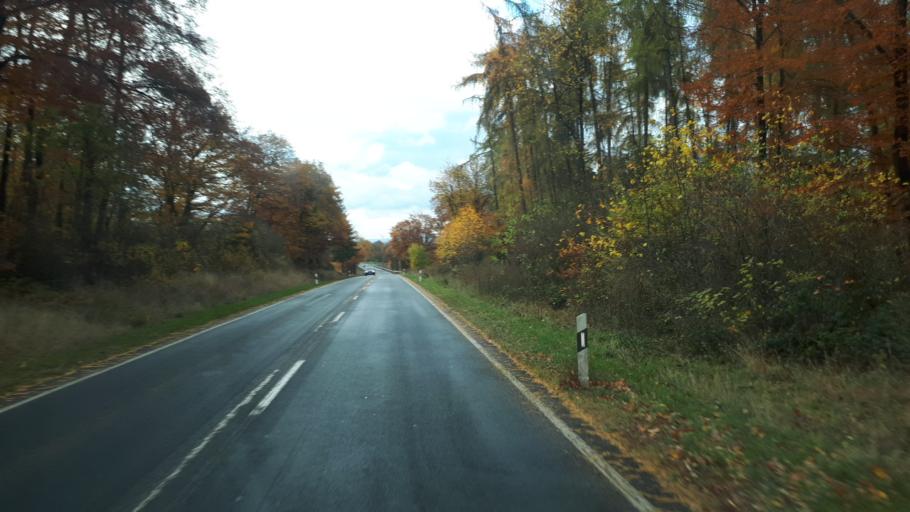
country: DE
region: Rheinland-Pfalz
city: Eulgem
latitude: 50.2272
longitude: 7.1635
